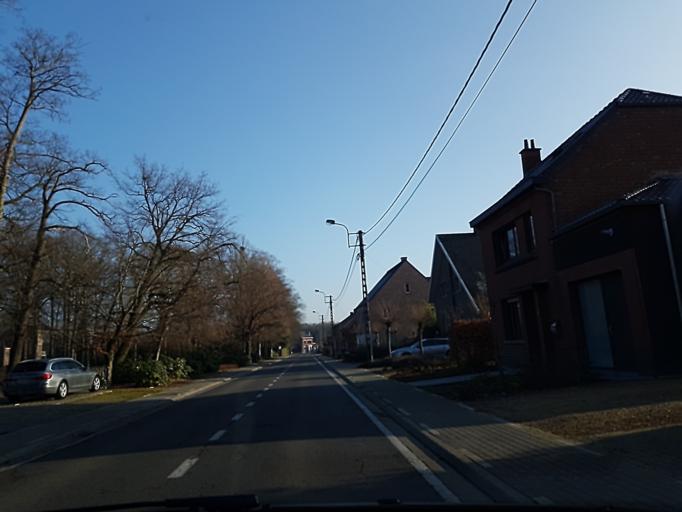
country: BE
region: Flanders
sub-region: Provincie Vlaams-Brabant
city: Haacht
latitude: 50.9697
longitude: 4.6359
